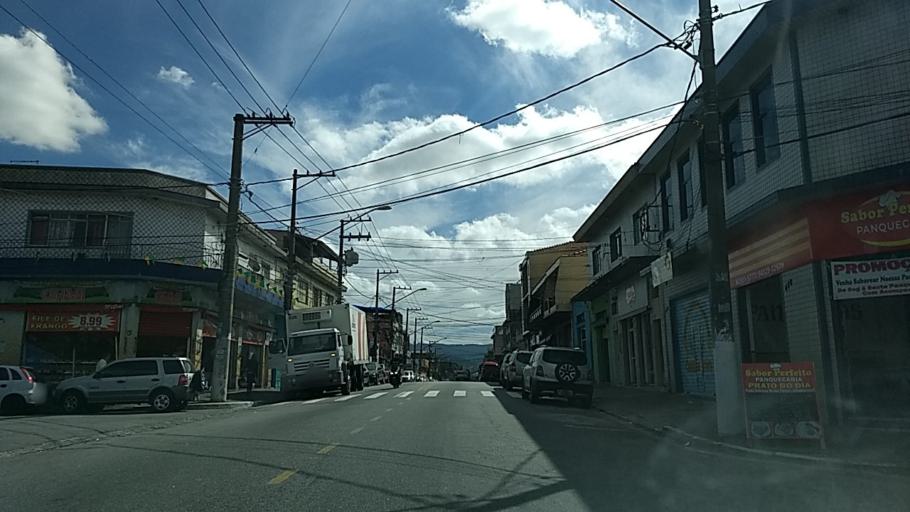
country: BR
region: Sao Paulo
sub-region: Guarulhos
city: Guarulhos
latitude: -23.4864
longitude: -46.5781
